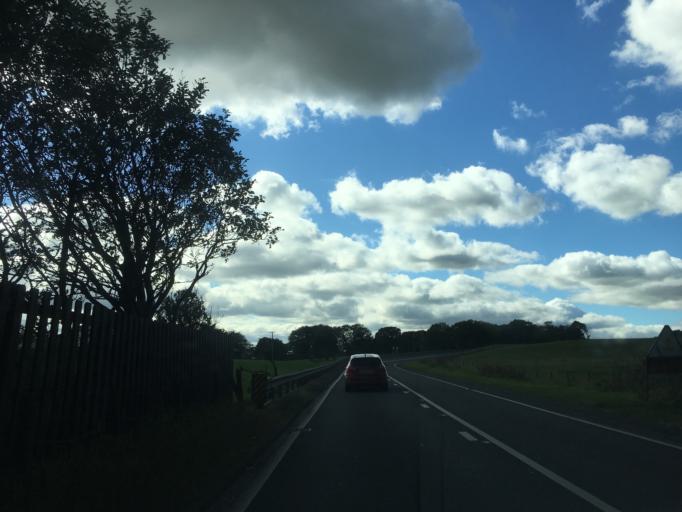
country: GB
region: Scotland
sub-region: Midlothian
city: Penicuik
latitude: 55.8440
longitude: -3.2392
